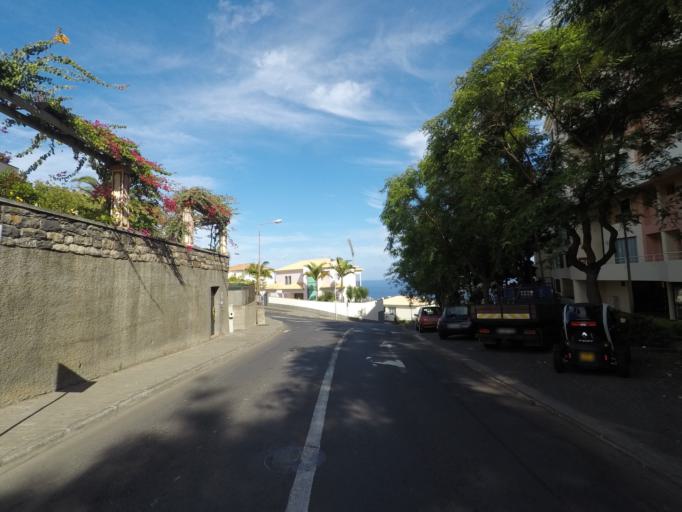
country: PT
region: Madeira
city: Camara de Lobos
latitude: 32.6386
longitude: -16.9414
